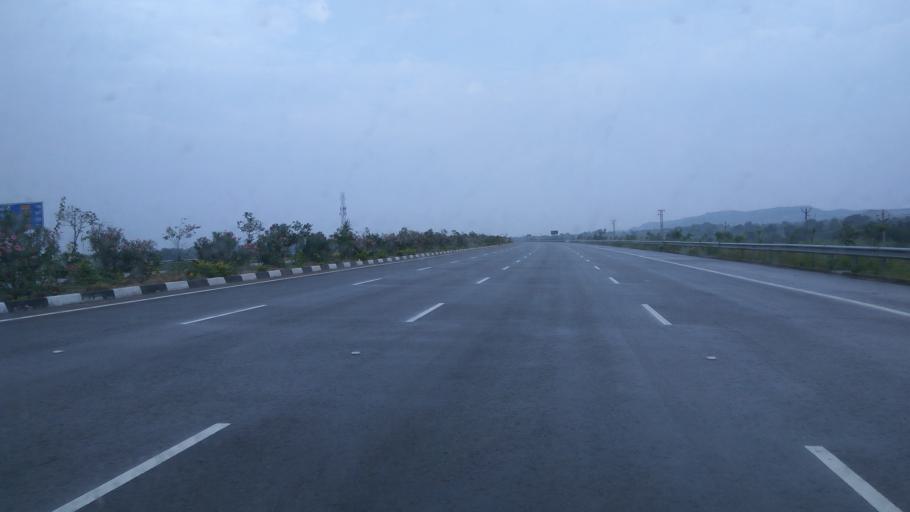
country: IN
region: Telangana
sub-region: Rangareddi
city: Ghatkesar
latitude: 17.4655
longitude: 78.6706
